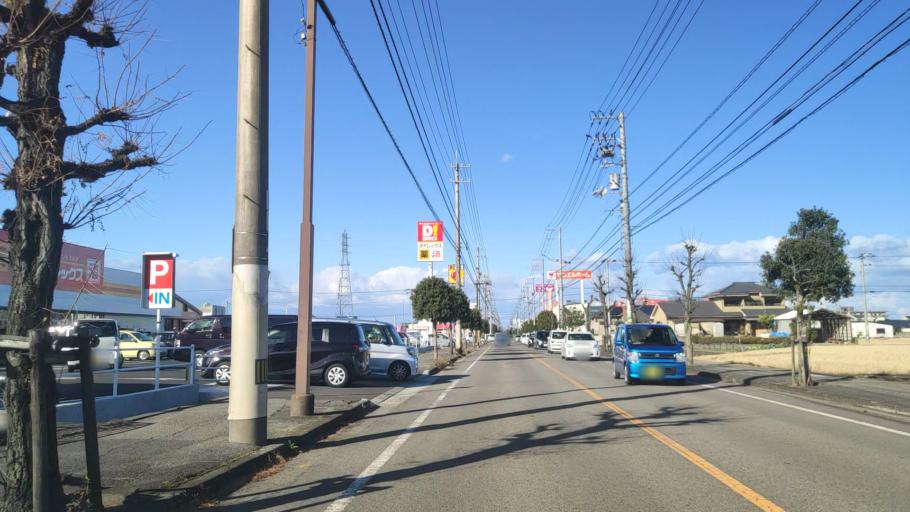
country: JP
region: Ehime
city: Saijo
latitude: 33.9239
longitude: 133.1912
